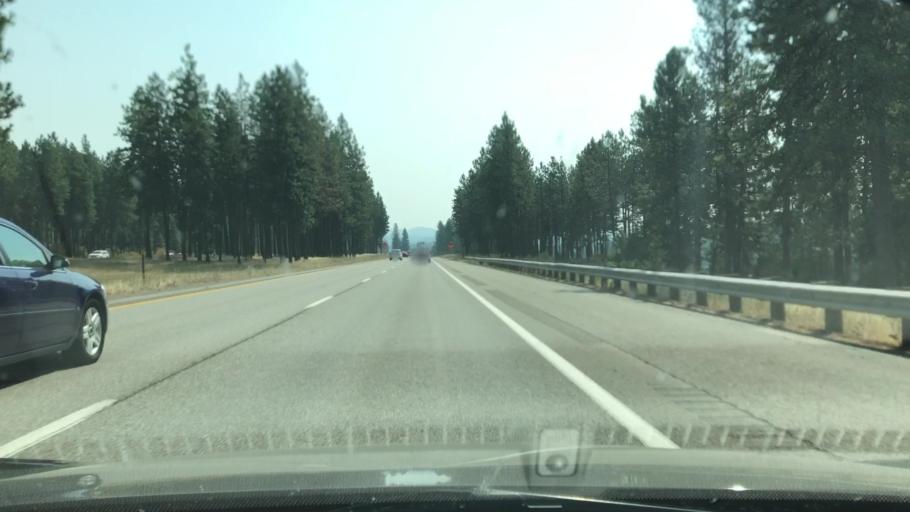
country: US
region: Idaho
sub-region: Kootenai County
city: Coeur d'Alene
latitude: 47.7064
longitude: -116.8465
